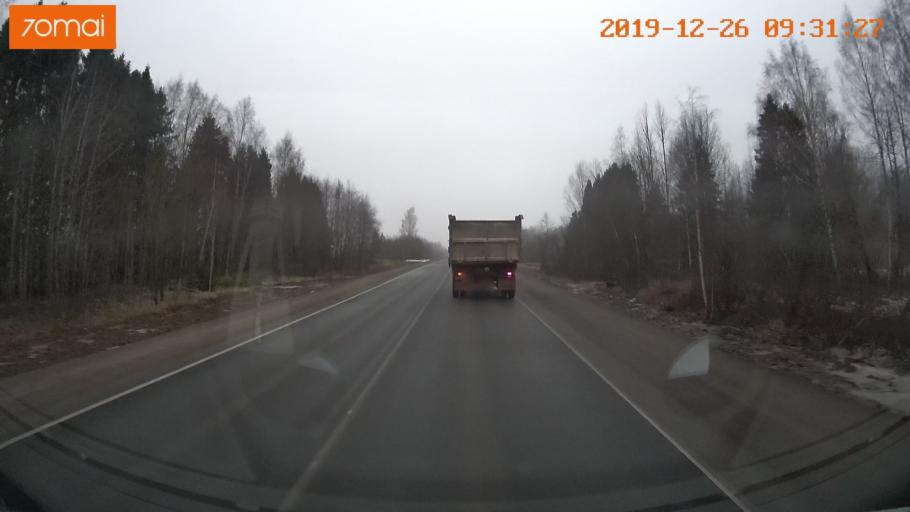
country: RU
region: Vologda
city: Gryazovets
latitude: 59.0693
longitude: 40.1277
